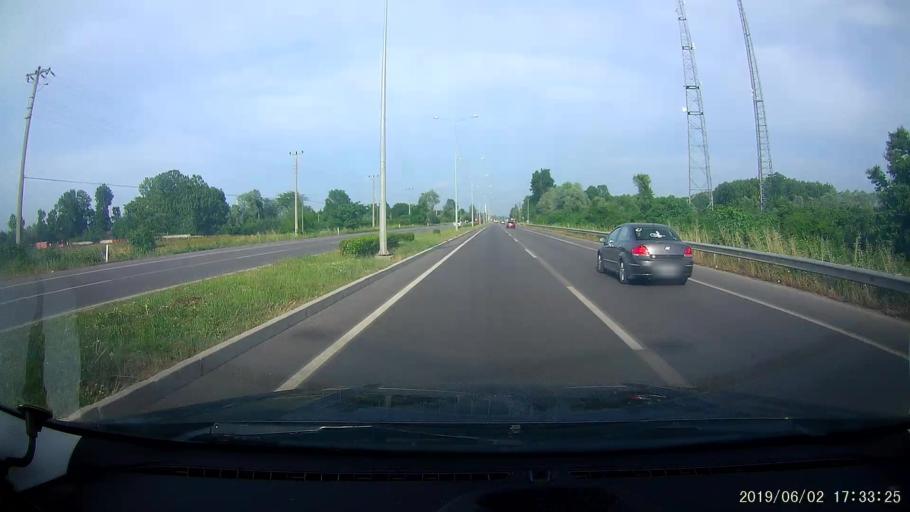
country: TR
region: Samsun
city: Terme
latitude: 41.2208
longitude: 36.8481
